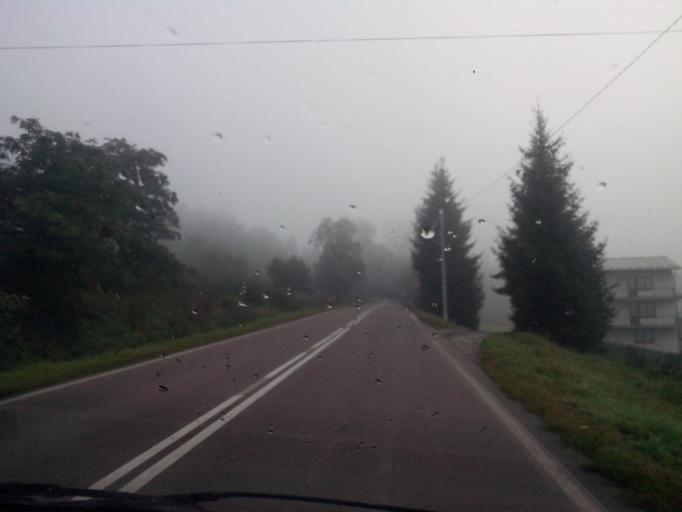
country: PL
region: Subcarpathian Voivodeship
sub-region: Powiat brzozowski
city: Domaradz
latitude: 49.7959
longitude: 21.9500
